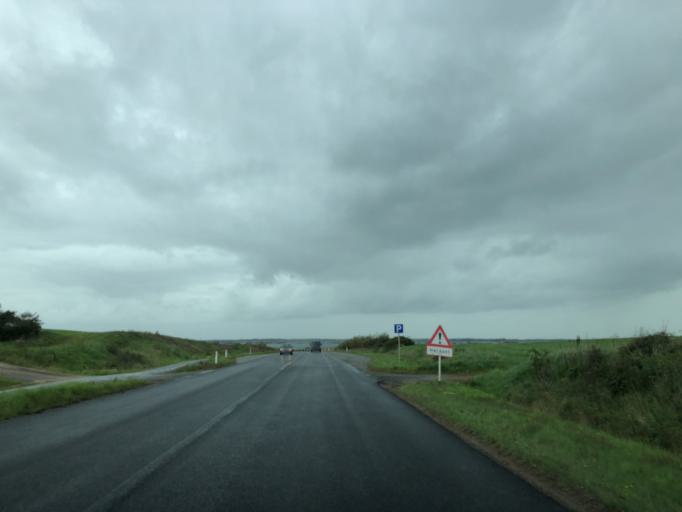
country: DK
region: Central Jutland
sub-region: Struer Kommune
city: Struer
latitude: 56.5539
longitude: 8.5581
